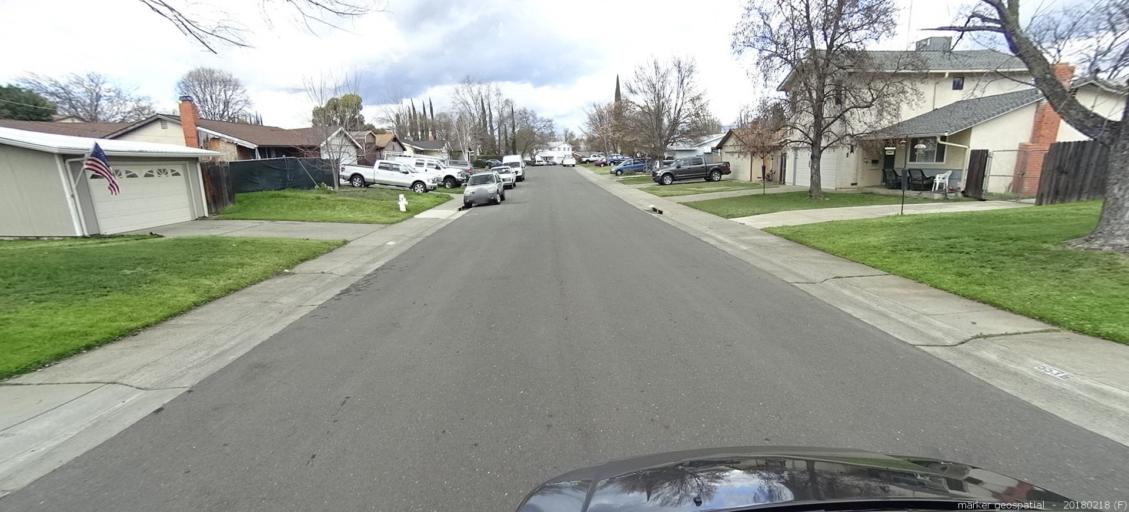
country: US
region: California
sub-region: Sacramento County
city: Orangevale
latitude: 38.6672
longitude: -121.2174
